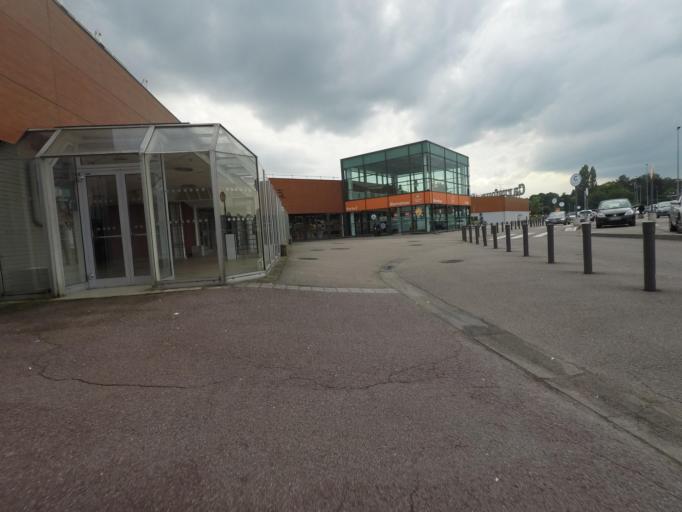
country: FR
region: Haute-Normandie
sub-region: Departement de la Seine-Maritime
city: Mont-Saint-Aignan
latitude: 49.4709
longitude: 1.0954
